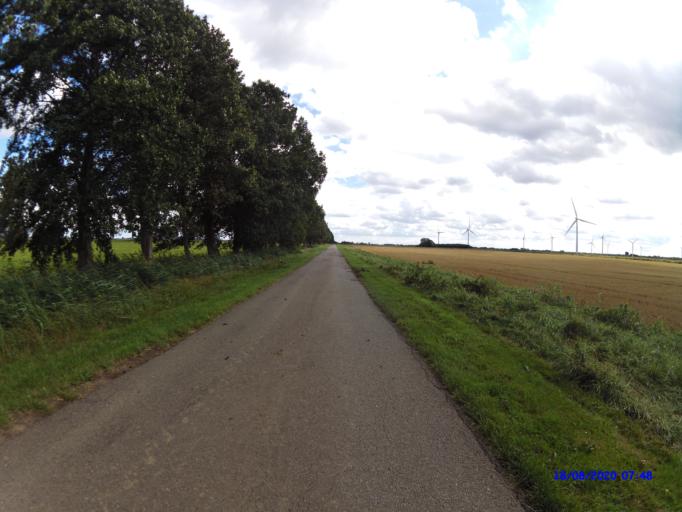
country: GB
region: England
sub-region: Cambridgeshire
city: Whittlesey
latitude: 52.5230
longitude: -0.0982
